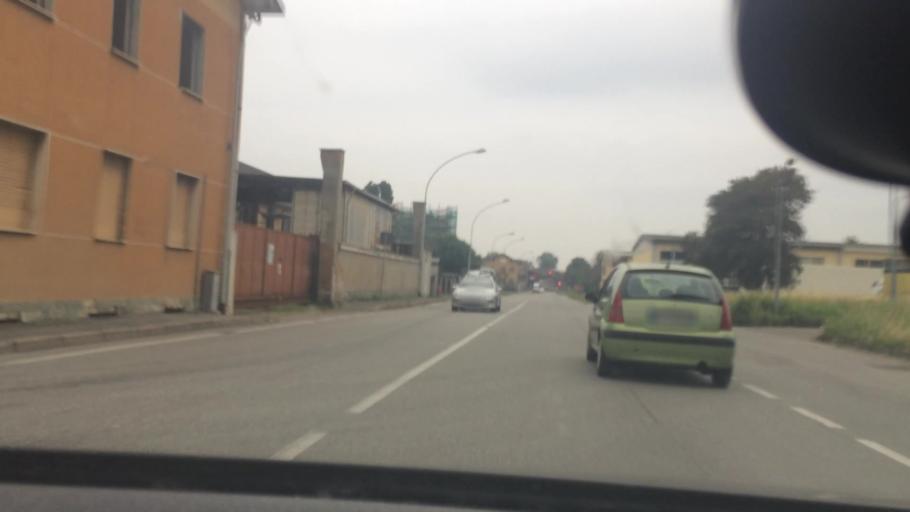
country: IT
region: Lombardy
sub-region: Citta metropolitana di Milano
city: Pero
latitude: 45.5049
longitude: 9.0762
